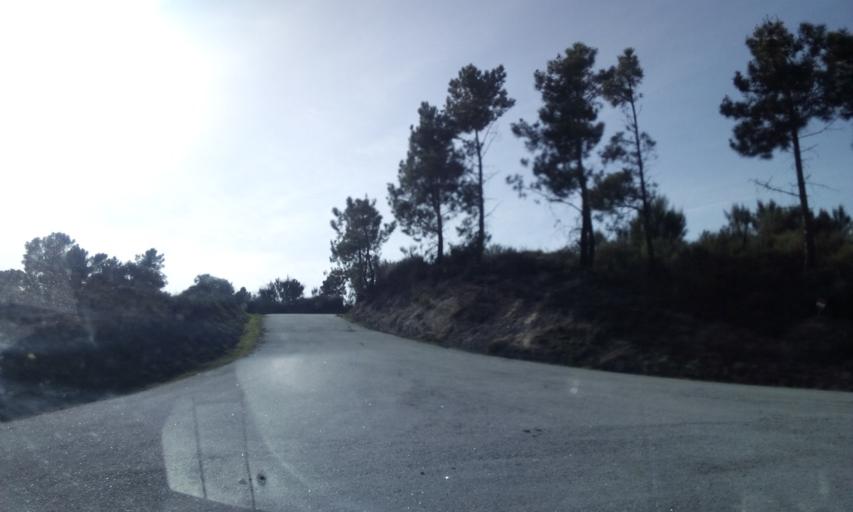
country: PT
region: Guarda
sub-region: Celorico da Beira
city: Celorico da Beira
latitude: 40.6547
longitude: -7.4001
